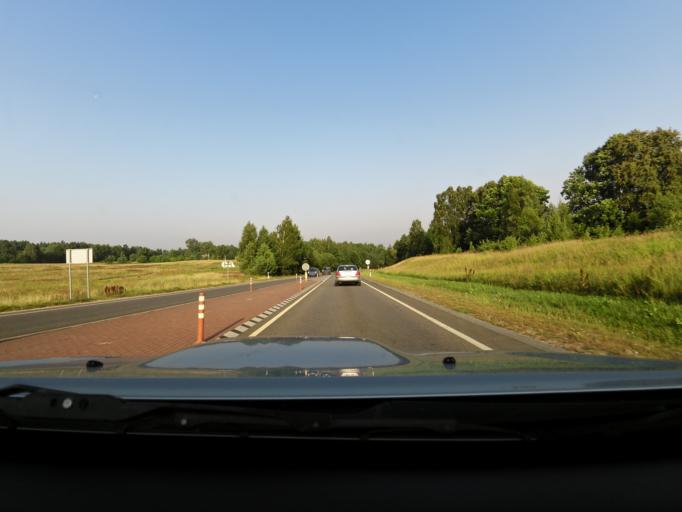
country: LT
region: Alytaus apskritis
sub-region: Alytus
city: Alytus
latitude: 54.3655
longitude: 24.1021
